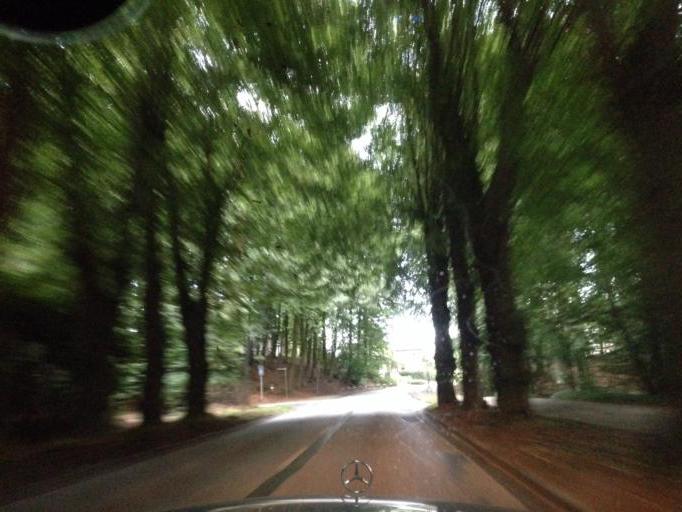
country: DE
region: Hamburg
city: Wohldorf-Ohlstedt
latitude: 53.6974
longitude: 10.1280
